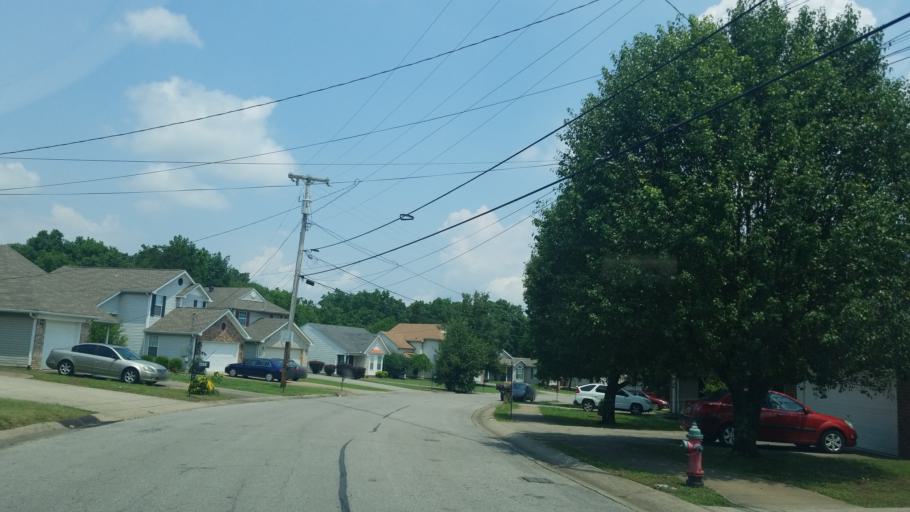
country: US
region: Tennessee
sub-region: Rutherford County
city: La Vergne
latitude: 36.0414
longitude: -86.5829
